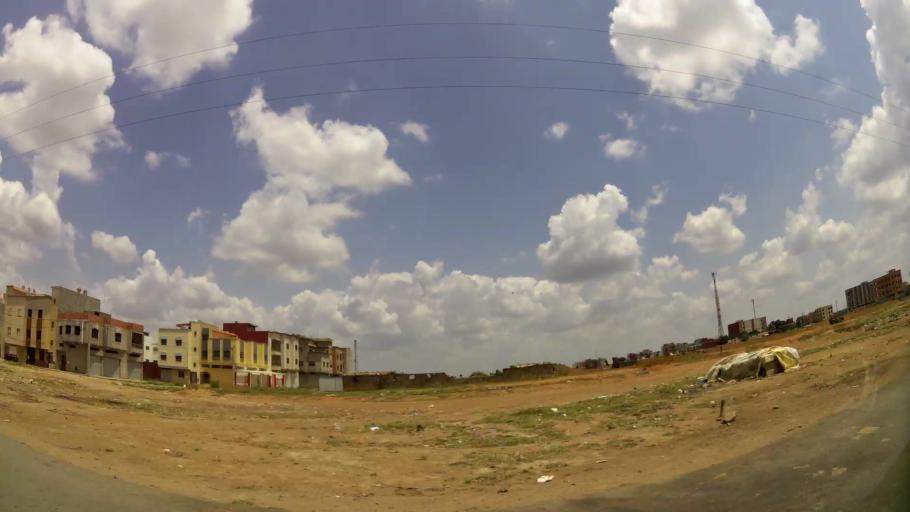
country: MA
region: Rabat-Sale-Zemmour-Zaer
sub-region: Khemisset
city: Tiflet
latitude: 34.0027
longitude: -6.5257
